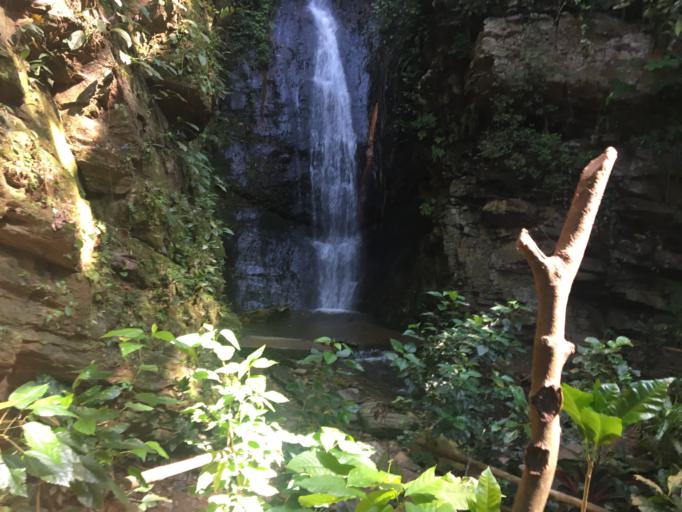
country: TG
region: Plateaux
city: Kpalime
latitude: 6.9516
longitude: 0.5976
